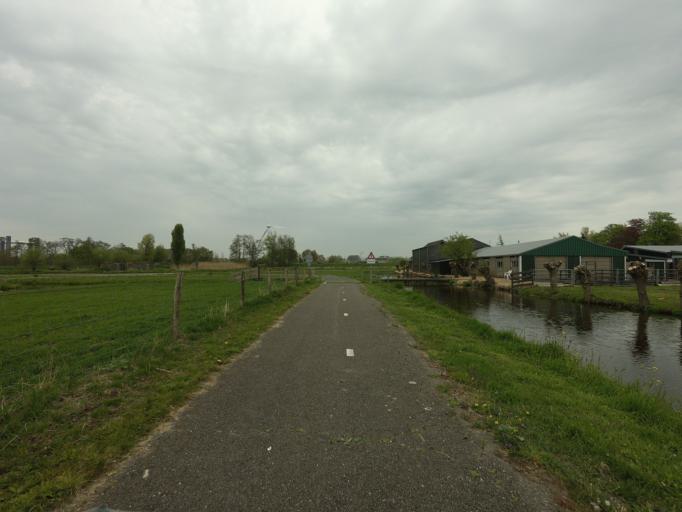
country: NL
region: South Holland
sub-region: Gemeente Gouda
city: Bloemendaal
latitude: 52.0118
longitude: 4.6823
